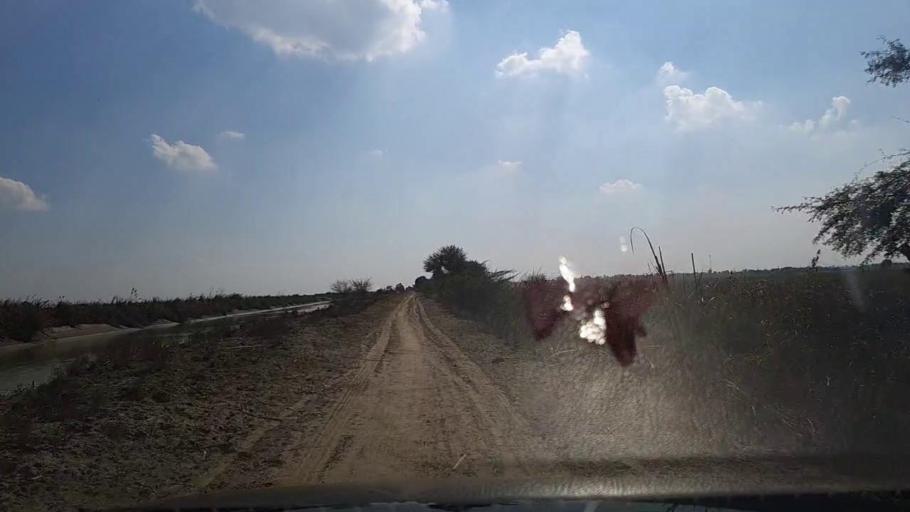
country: PK
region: Sindh
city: Tando Mittha Khan
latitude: 25.8444
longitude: 69.0743
